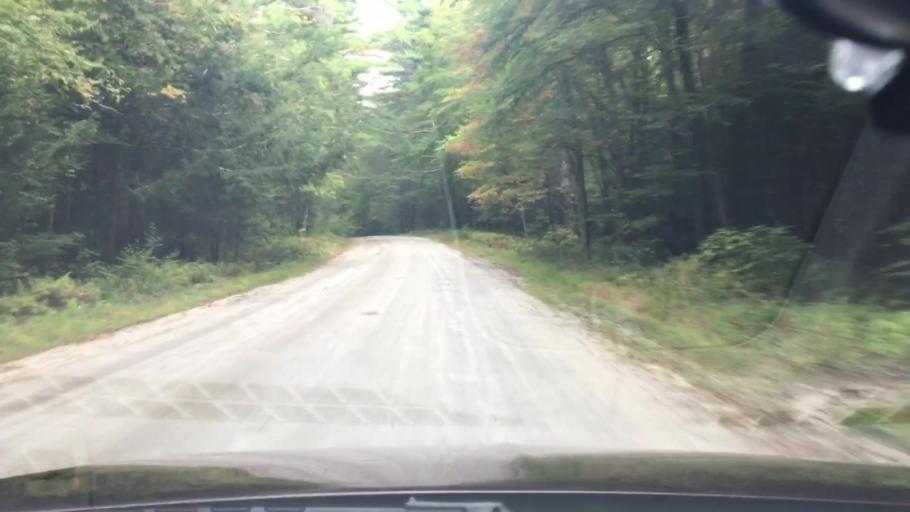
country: US
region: Connecticut
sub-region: Tolland County
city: Stafford
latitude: 41.9895
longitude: -72.3306
